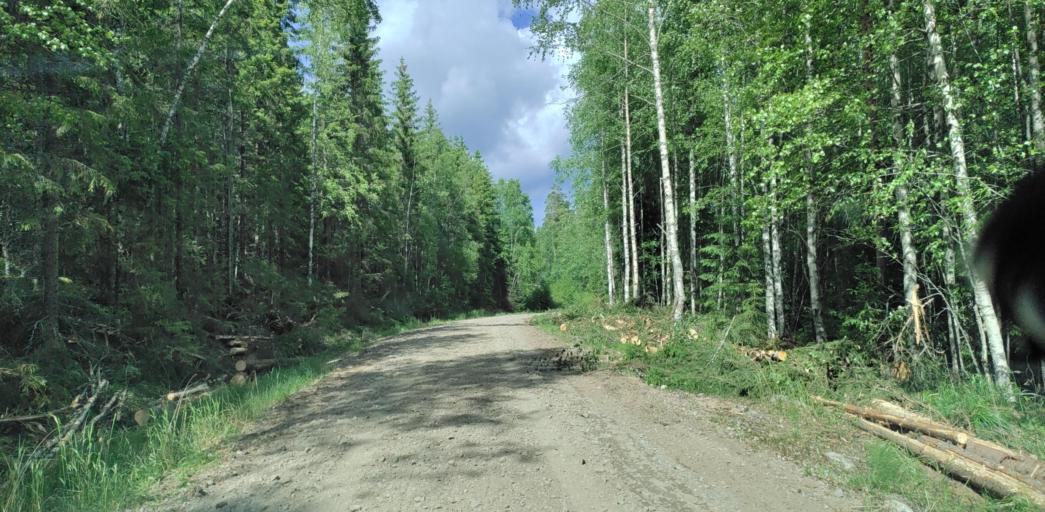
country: SE
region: Vaermland
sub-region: Munkfors Kommun
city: Munkfors
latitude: 59.9697
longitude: 13.4067
